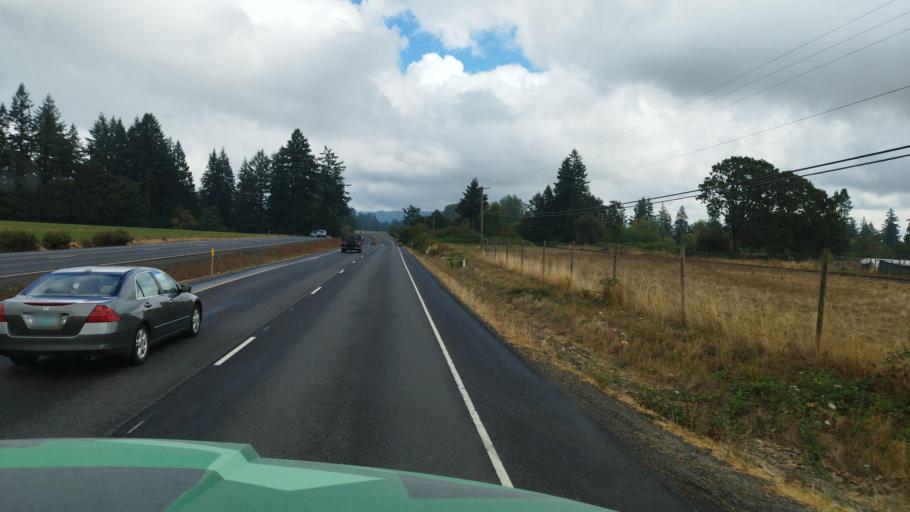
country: US
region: Oregon
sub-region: Yamhill County
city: Lafayette
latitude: 45.2402
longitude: -123.1388
